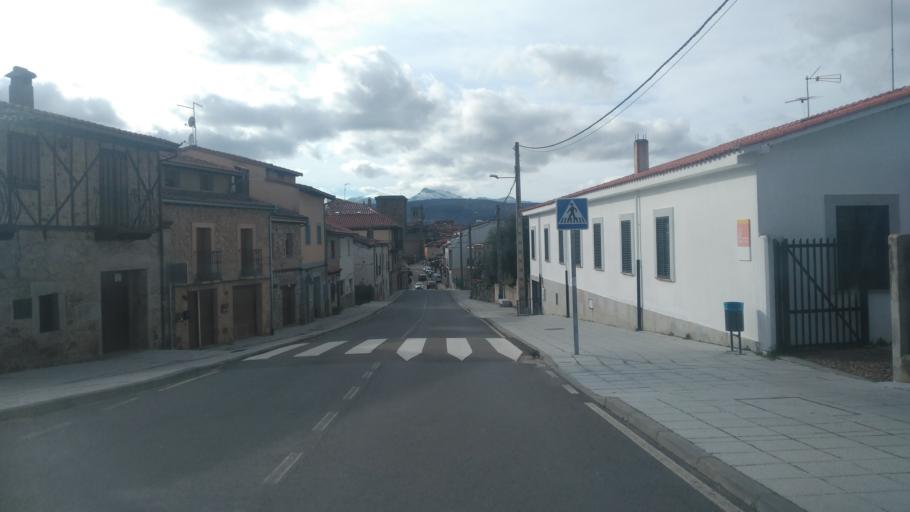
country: ES
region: Castille and Leon
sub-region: Provincia de Salamanca
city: Miranda del Castanar
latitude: 40.4840
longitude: -5.9955
